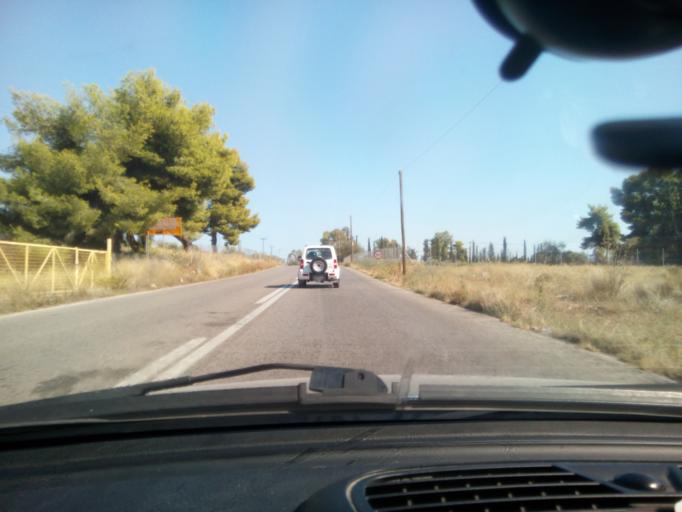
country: GR
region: Central Greece
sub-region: Nomos Evvoias
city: Malakonta
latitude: 38.4076
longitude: 23.7305
